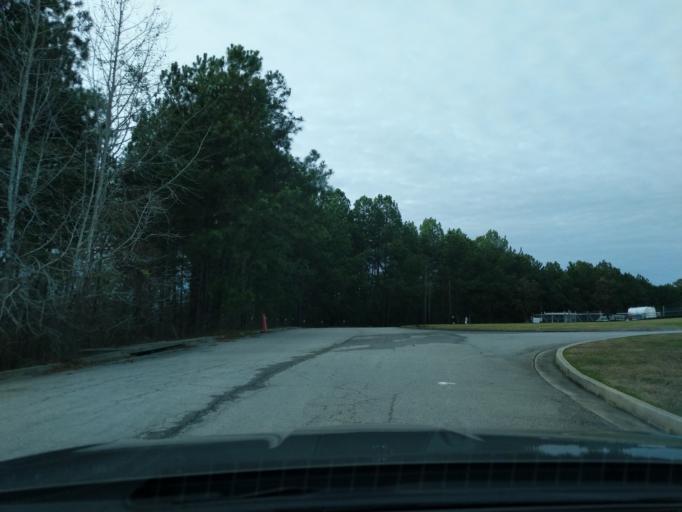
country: US
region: Georgia
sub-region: Columbia County
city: Grovetown
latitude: 33.4692
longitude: -82.1954
